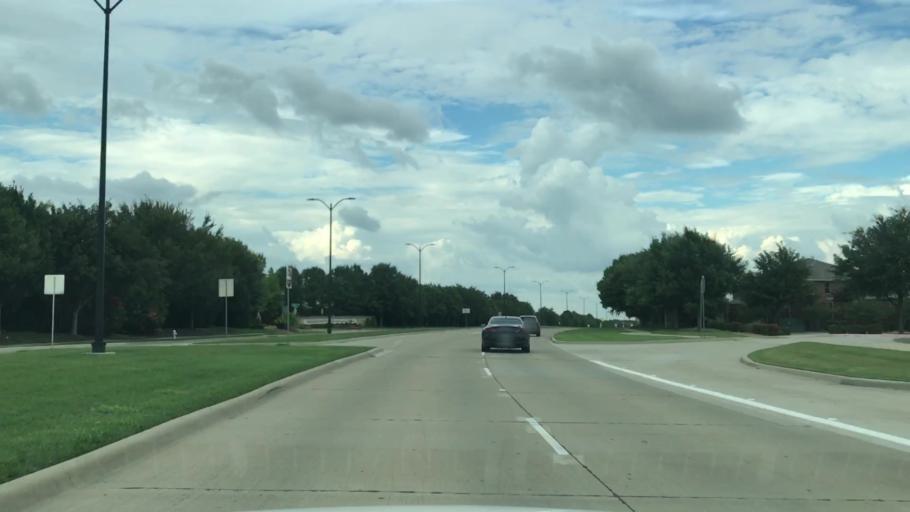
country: US
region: Texas
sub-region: Collin County
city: Frisco
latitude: 33.1754
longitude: -96.7856
